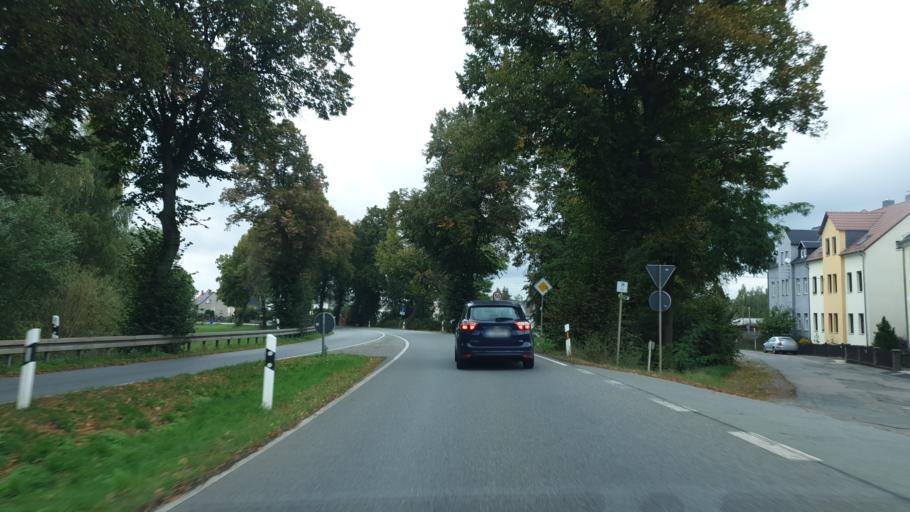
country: DE
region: Saxony
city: Glauchau
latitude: 50.8305
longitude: 12.5559
